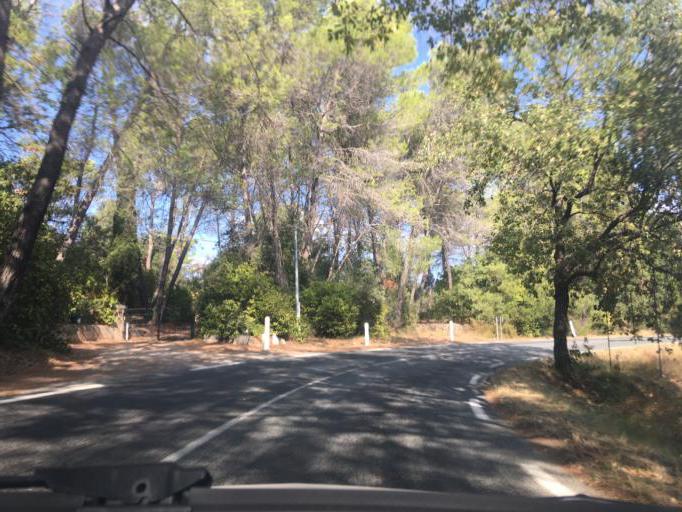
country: FR
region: Provence-Alpes-Cote d'Azur
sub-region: Departement du Var
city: Flayosc
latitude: 43.4988
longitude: 6.4153
